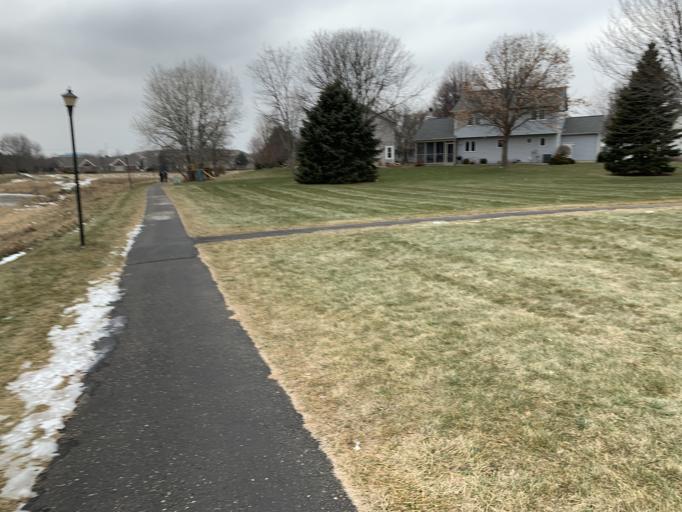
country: US
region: Wisconsin
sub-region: Dane County
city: Middleton
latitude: 43.0777
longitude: -89.5143
